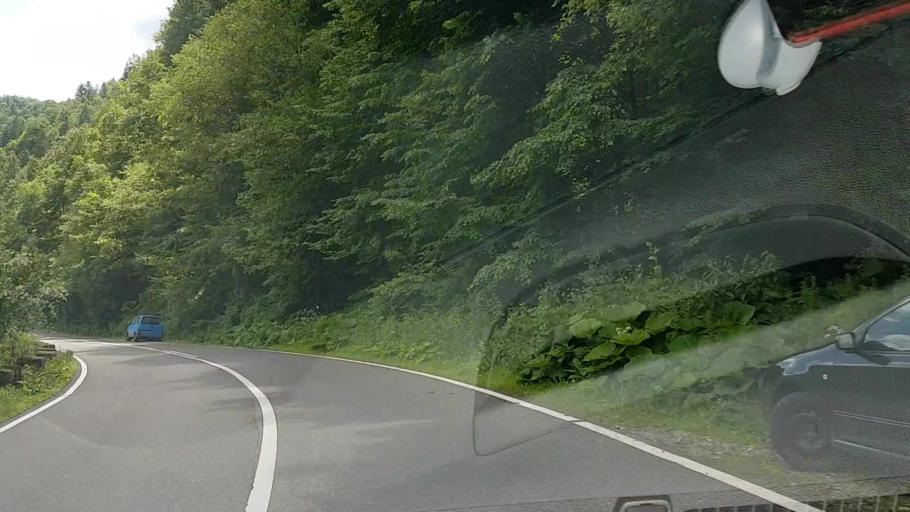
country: RO
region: Suceava
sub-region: Comuna Crucea
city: Crucea
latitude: 47.3147
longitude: 25.6252
